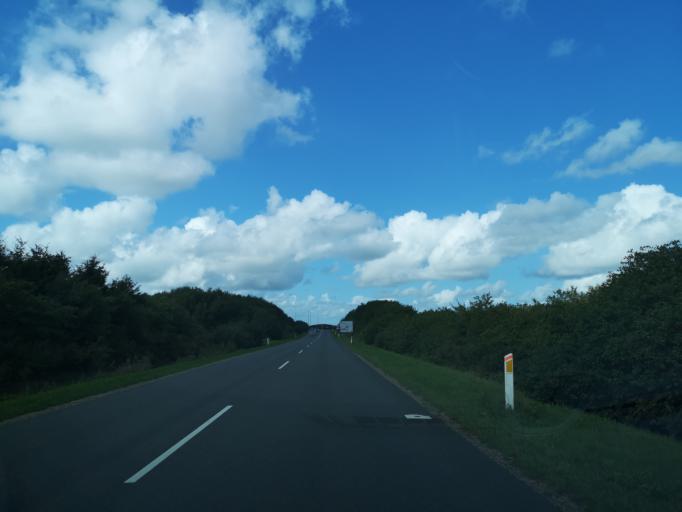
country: DK
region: Central Jutland
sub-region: Holstebro Kommune
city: Holstebro
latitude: 56.3889
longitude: 8.6027
